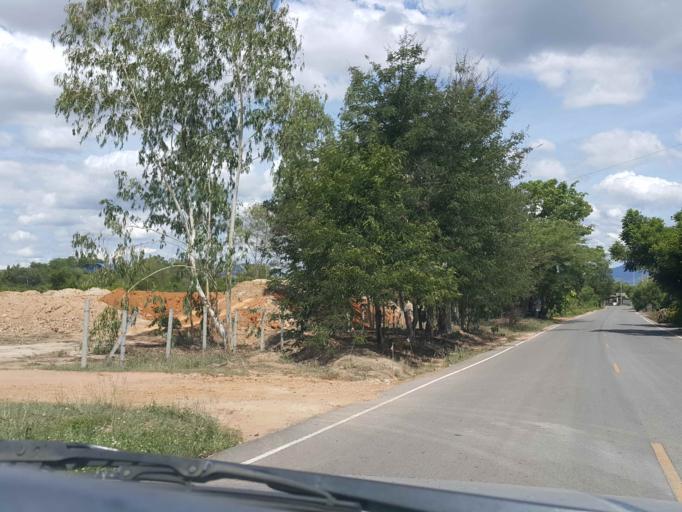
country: TH
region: Chiang Mai
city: Doi Lo
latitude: 18.4588
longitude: 98.7663
